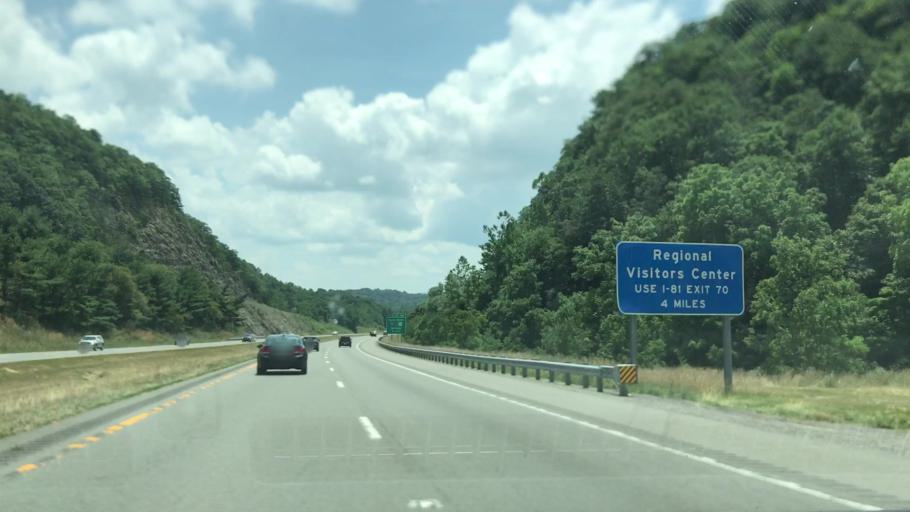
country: US
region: Virginia
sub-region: Wythe County
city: Wytheville
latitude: 36.9945
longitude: -81.0804
